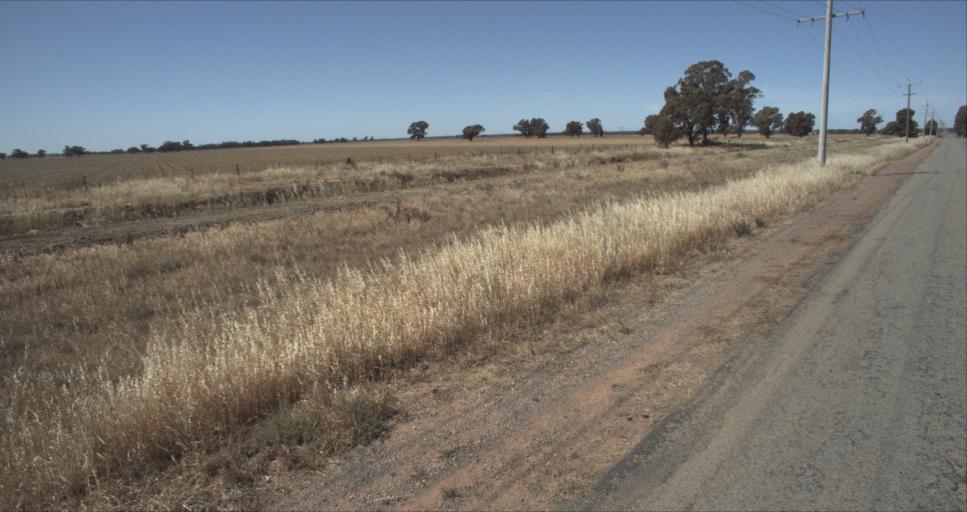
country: AU
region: New South Wales
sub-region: Leeton
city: Leeton
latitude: -34.5697
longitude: 146.3109
